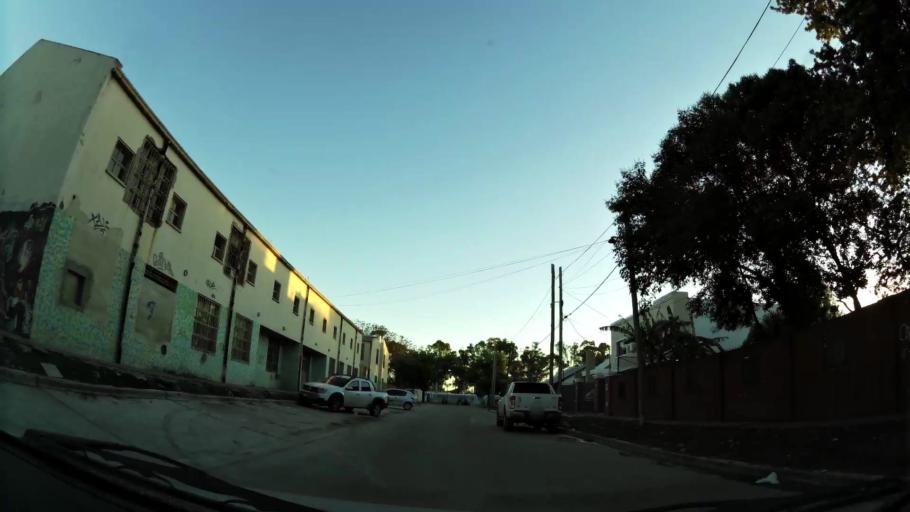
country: AR
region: Buenos Aires
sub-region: Partido de Almirante Brown
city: Adrogue
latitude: -34.7996
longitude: -58.3396
